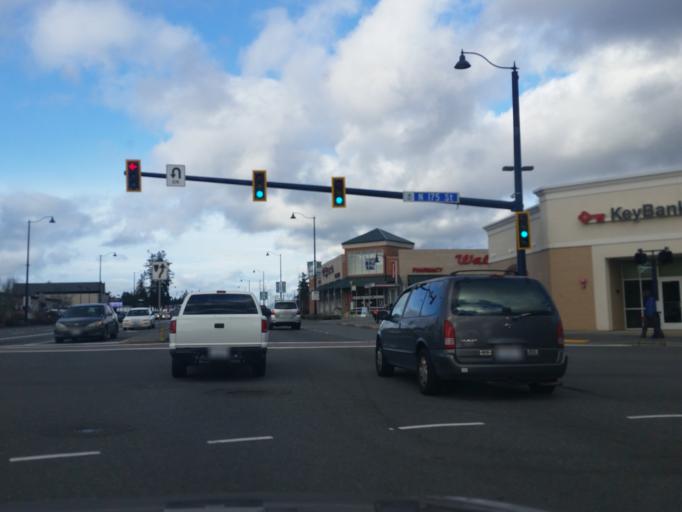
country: US
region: Washington
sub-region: King County
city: Shoreline
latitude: 47.7559
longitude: -122.3456
